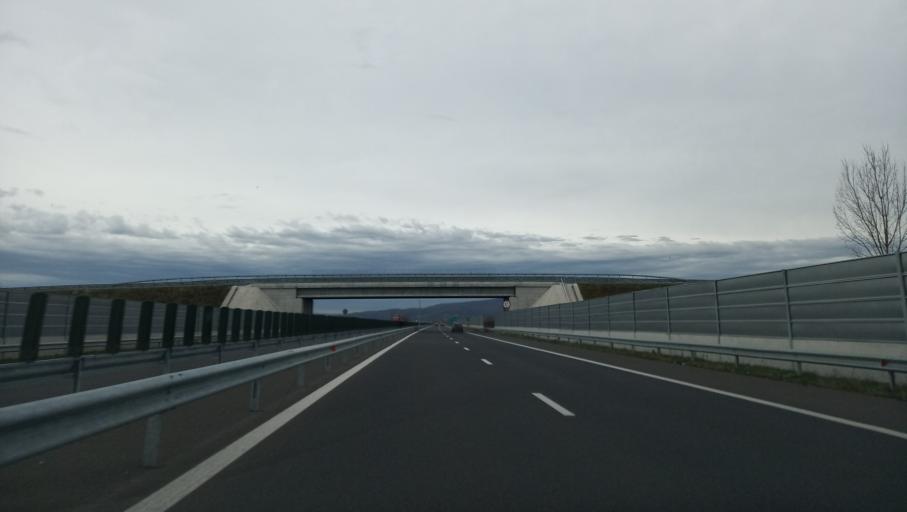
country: RO
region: Hunedoara
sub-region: Comuna Ilia
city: Ilia
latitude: 45.9466
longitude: 22.6696
